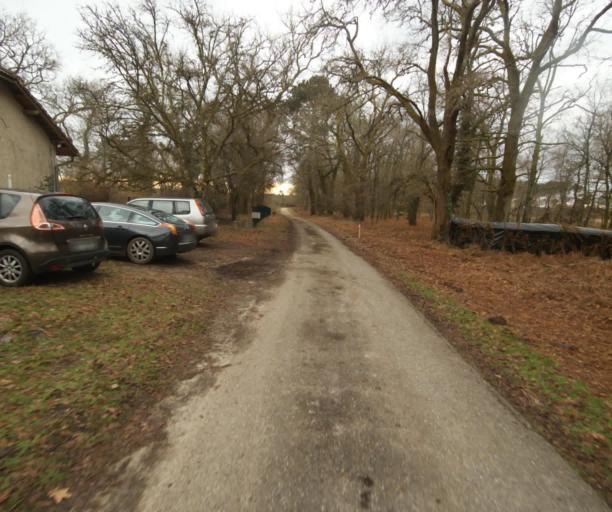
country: FR
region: Aquitaine
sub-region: Departement des Landes
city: Gabarret
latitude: 44.0141
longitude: -0.0599
